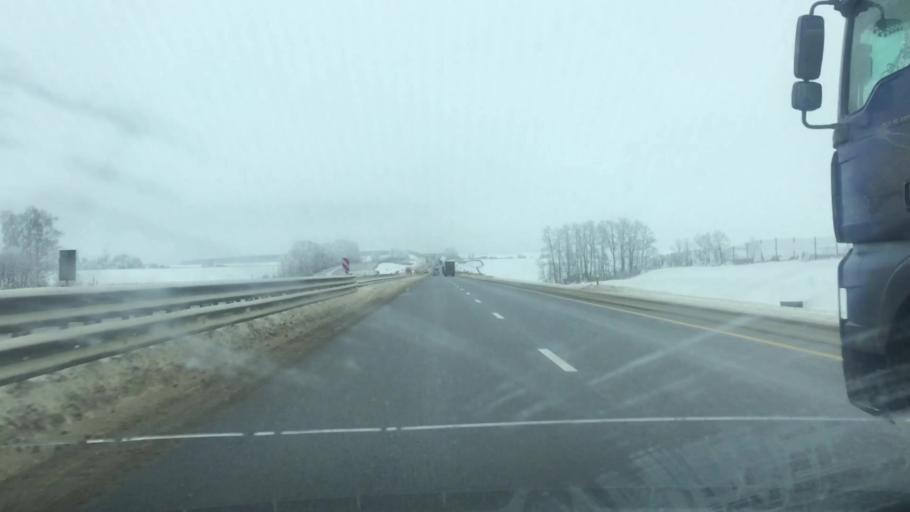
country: RU
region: Tula
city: Kazachka
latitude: 53.3327
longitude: 38.1805
